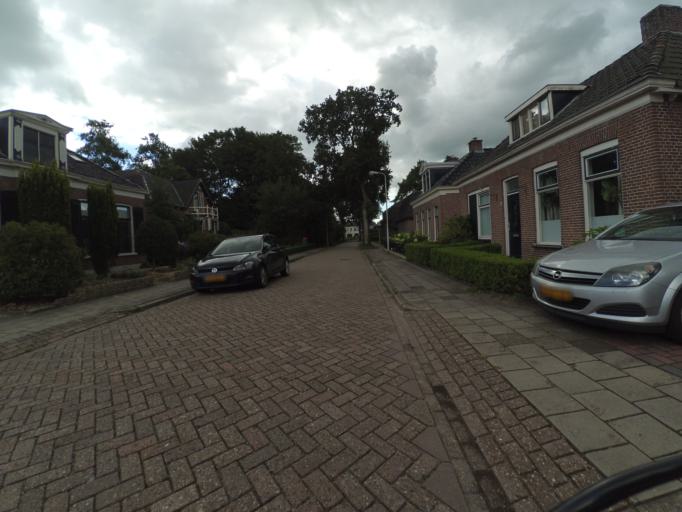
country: NL
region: Friesland
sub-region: Gemeente Tytsjerksteradiel
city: Hurdegaryp
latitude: 53.2191
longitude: 5.9400
